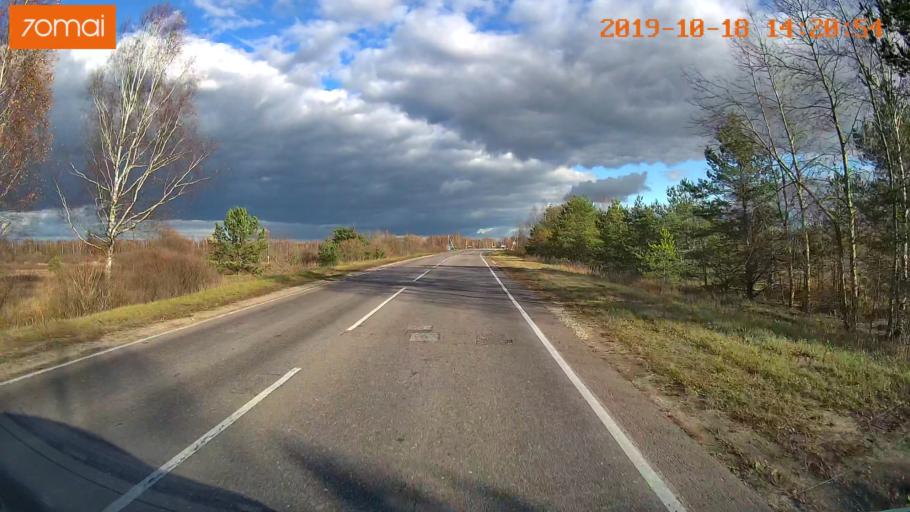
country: RU
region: Rjazan
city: Tuma
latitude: 55.1468
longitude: 40.4431
